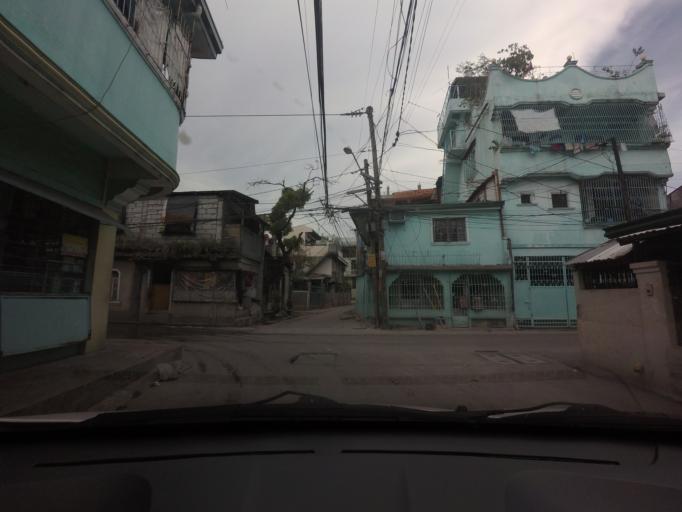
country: PH
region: Calabarzon
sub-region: Province of Rizal
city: Taguig
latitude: 14.5030
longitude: 121.0595
